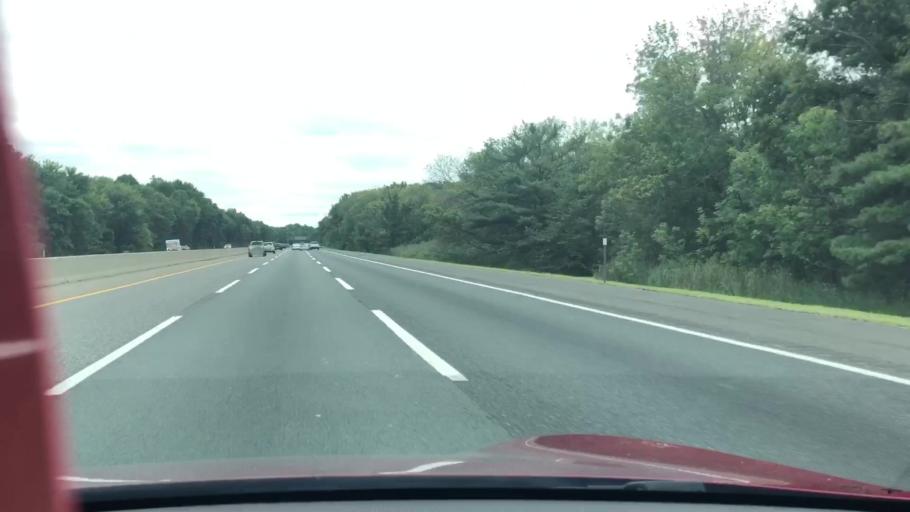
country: US
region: New Jersey
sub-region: Burlington County
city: Roebling
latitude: 40.0644
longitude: -74.7703
